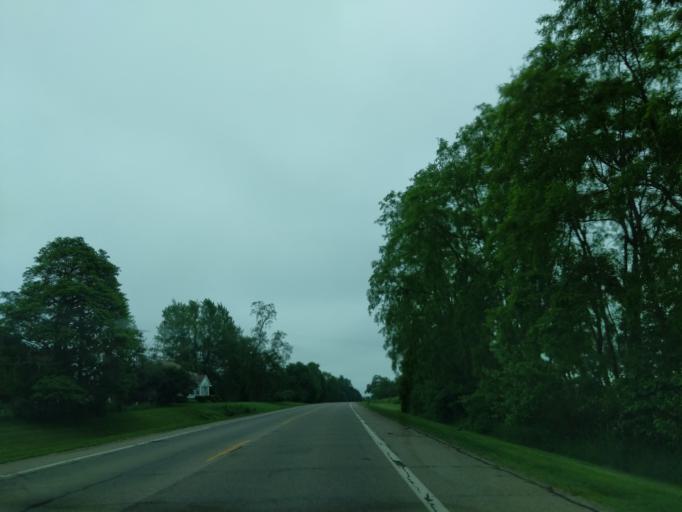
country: US
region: Michigan
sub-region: Hillsdale County
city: Jonesville
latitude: 42.0234
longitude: -84.6993
